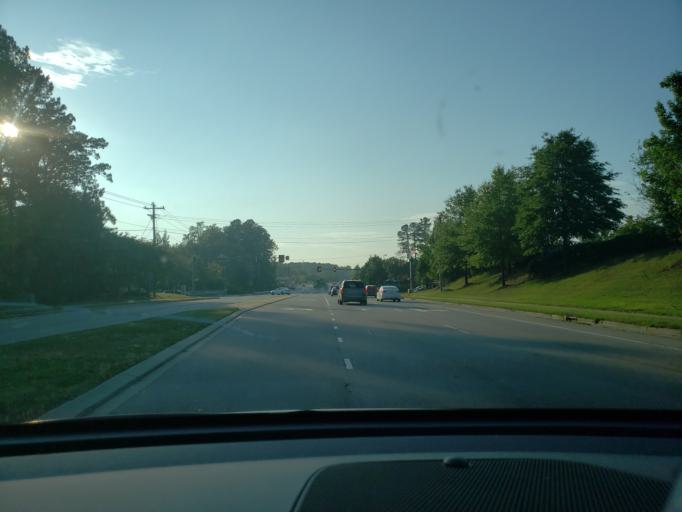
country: US
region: North Carolina
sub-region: Durham County
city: Durham
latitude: 35.9472
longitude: -78.9231
